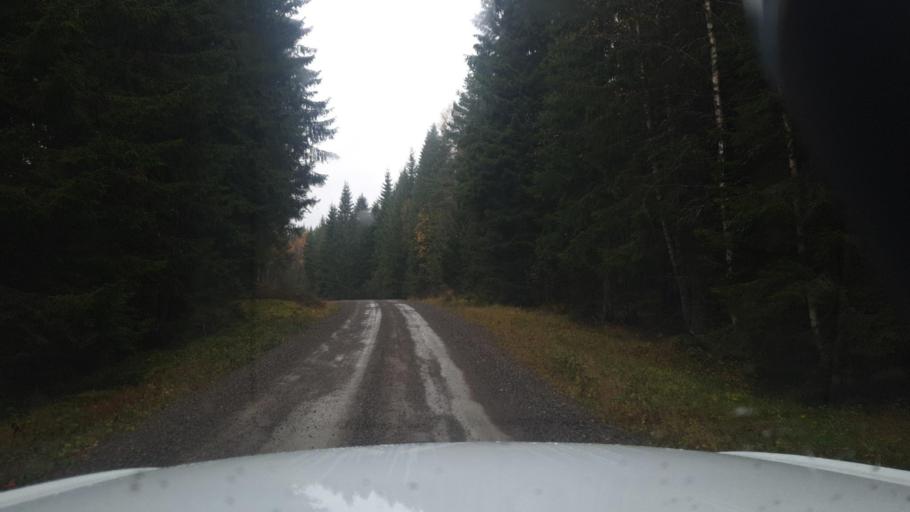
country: SE
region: Vaermland
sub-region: Eda Kommun
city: Charlottenberg
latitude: 60.0281
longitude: 12.6339
